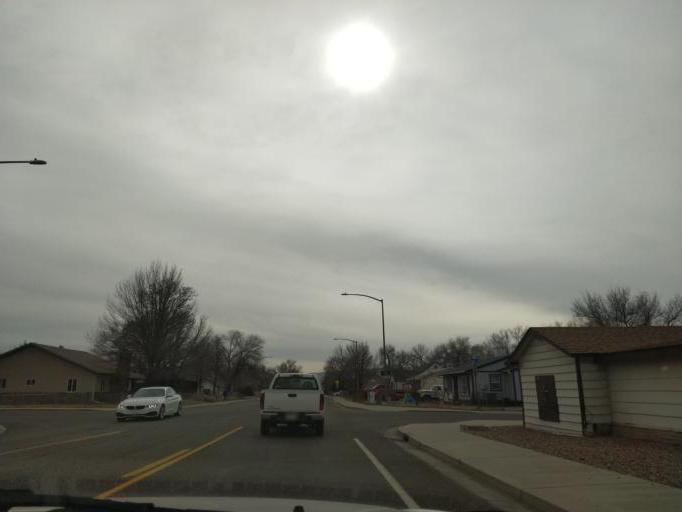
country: US
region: Colorado
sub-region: Mesa County
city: Grand Junction
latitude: 39.0823
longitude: -108.5292
